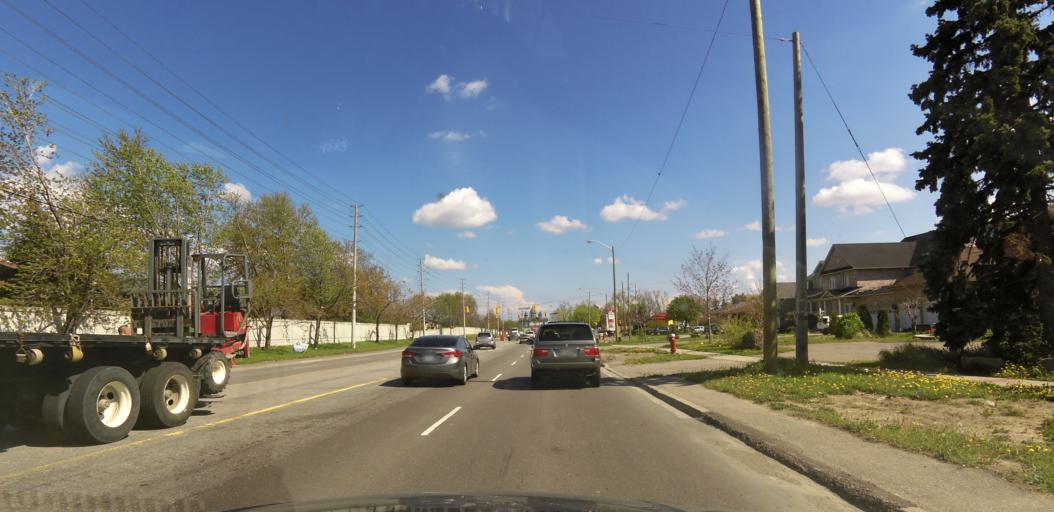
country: CA
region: Ontario
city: Mississauga
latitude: 43.6113
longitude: -79.6230
